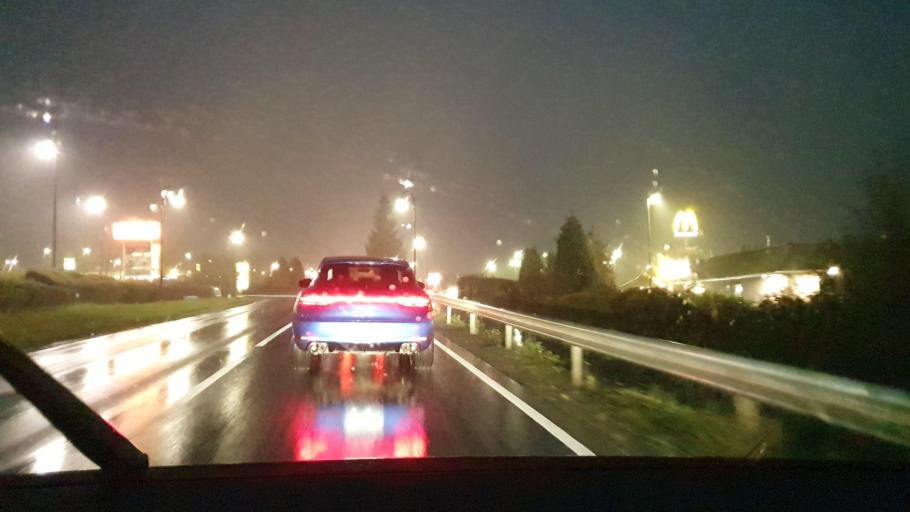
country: DE
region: Rheinland-Pfalz
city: Rennerod
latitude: 50.5984
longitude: 8.0633
